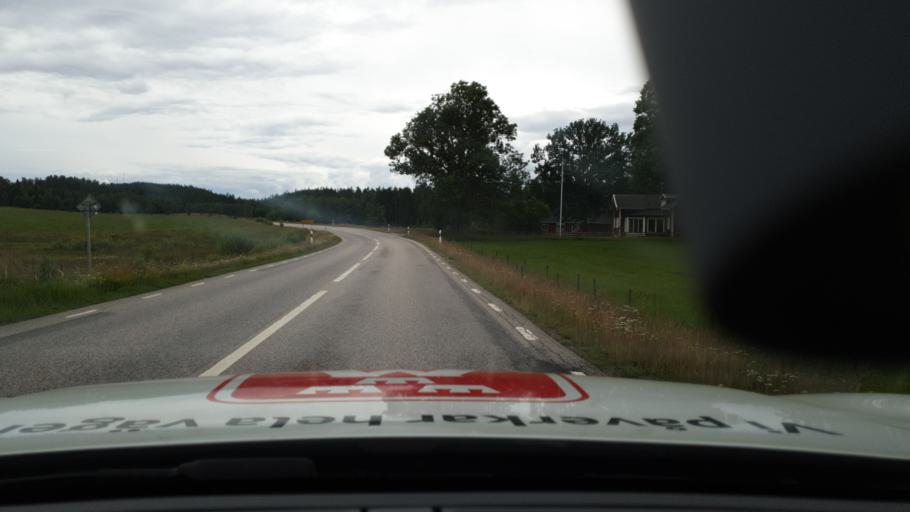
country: SE
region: Joenkoeping
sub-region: Varnamo Kommun
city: Bredaryd
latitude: 57.2425
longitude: 13.7778
